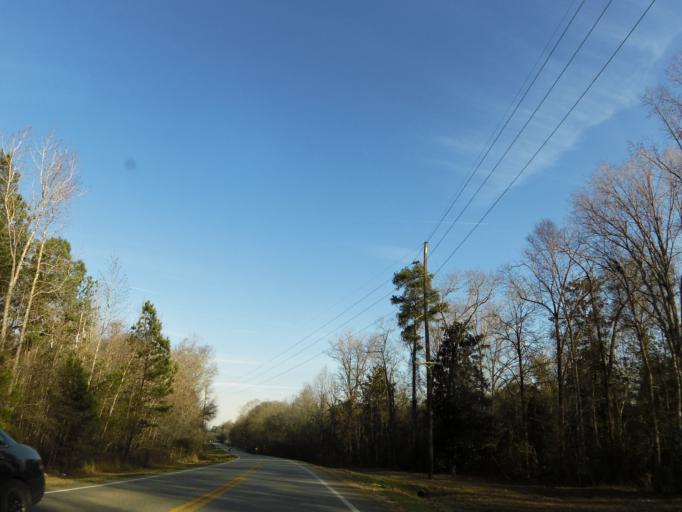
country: US
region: Georgia
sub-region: Webster County
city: Preston
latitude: 32.0344
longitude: -84.4726
